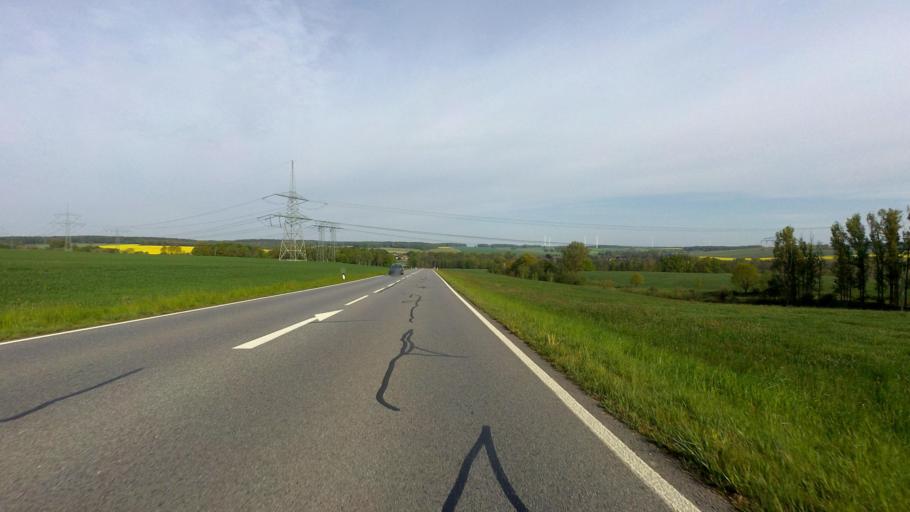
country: DE
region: Saxony
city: Stolpen
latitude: 51.0520
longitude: 14.0736
